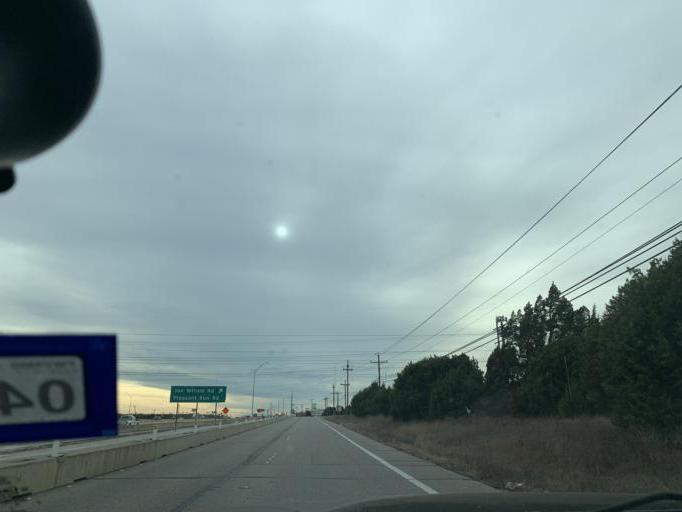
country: US
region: Texas
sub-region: Dallas County
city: Shamrock
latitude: 32.6144
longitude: -96.9210
